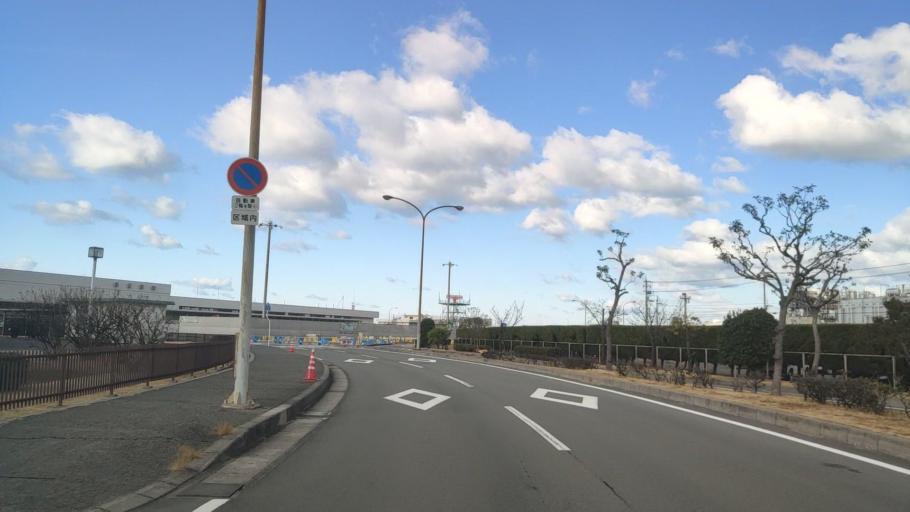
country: JP
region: Ehime
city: Masaki-cho
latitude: 33.8301
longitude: 132.7032
